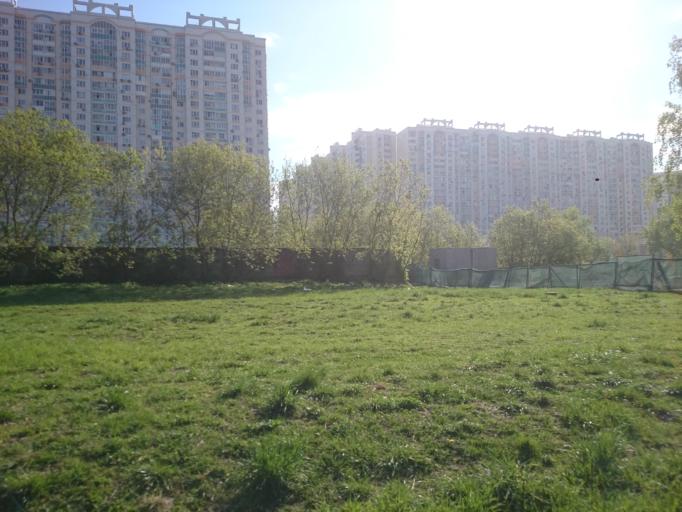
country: RU
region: Moscow
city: Tekstil'shchiki
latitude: 55.7172
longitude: 37.7427
